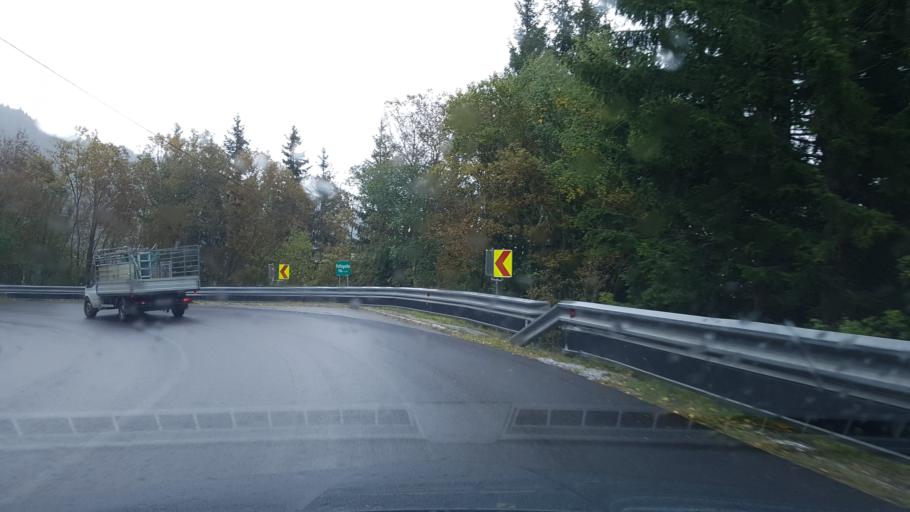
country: AT
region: Styria
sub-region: Politischer Bezirk Voitsberg
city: Salla
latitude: 47.1072
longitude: 14.9456
